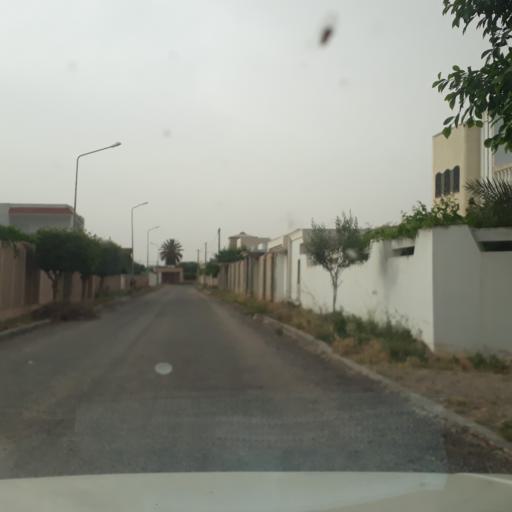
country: TN
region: Safaqis
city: Al Qarmadah
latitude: 34.8130
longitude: 10.7667
